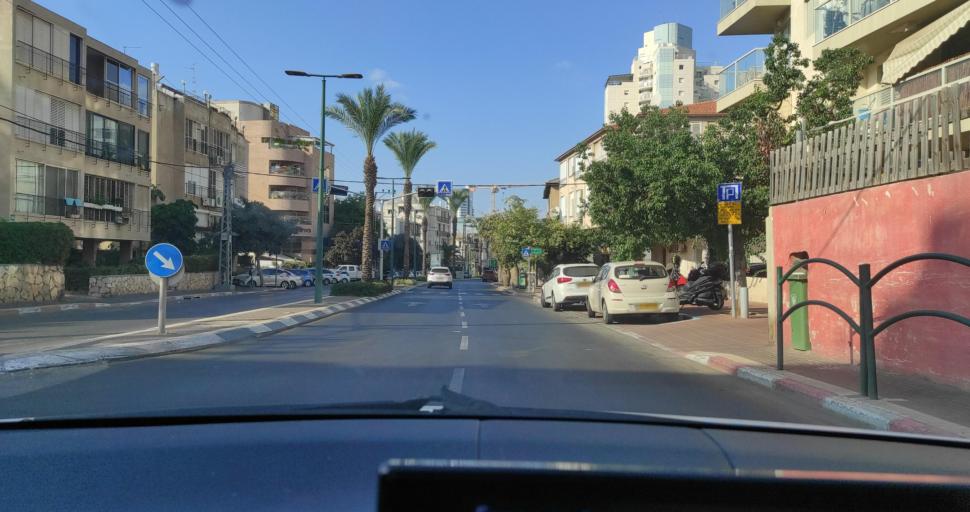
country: IL
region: Tel Aviv
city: Giv`atayim
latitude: 32.0728
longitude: 34.8184
